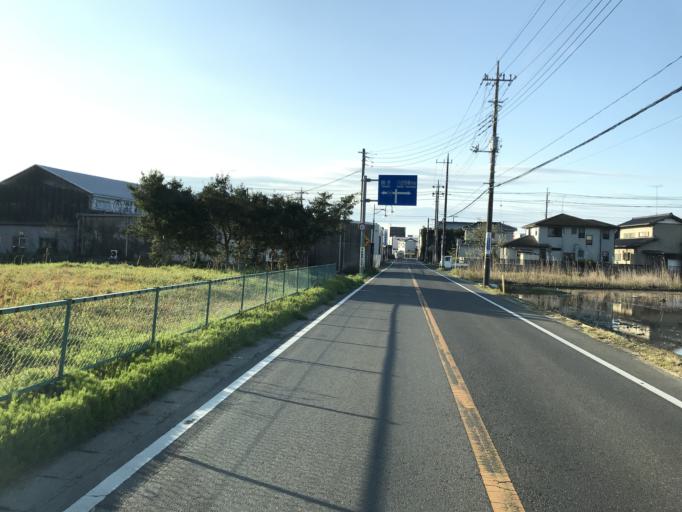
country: JP
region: Chiba
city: Yokaichiba
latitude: 35.7069
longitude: 140.5574
